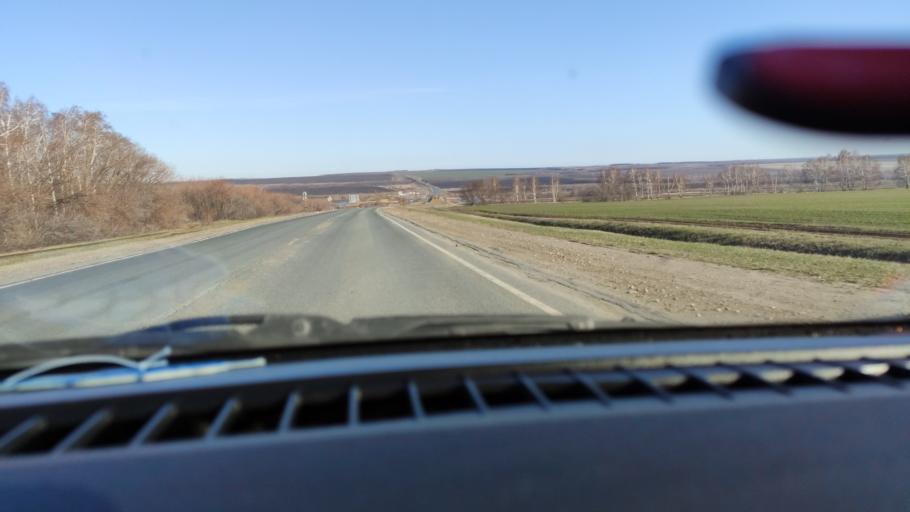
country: RU
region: Saratov
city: Dukhovnitskoye
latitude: 52.7258
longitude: 48.2610
